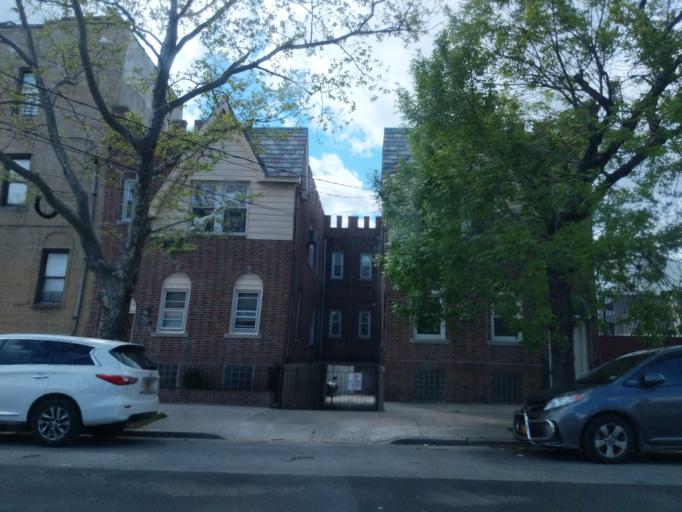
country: US
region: New York
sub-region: Bronx
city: The Bronx
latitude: 40.8650
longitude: -73.8616
